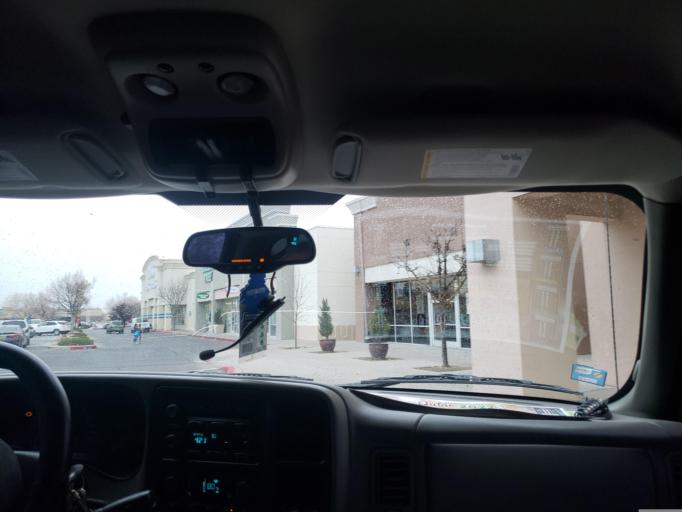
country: US
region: New Mexico
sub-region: Bernalillo County
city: North Valley
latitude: 35.1328
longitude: -106.5883
